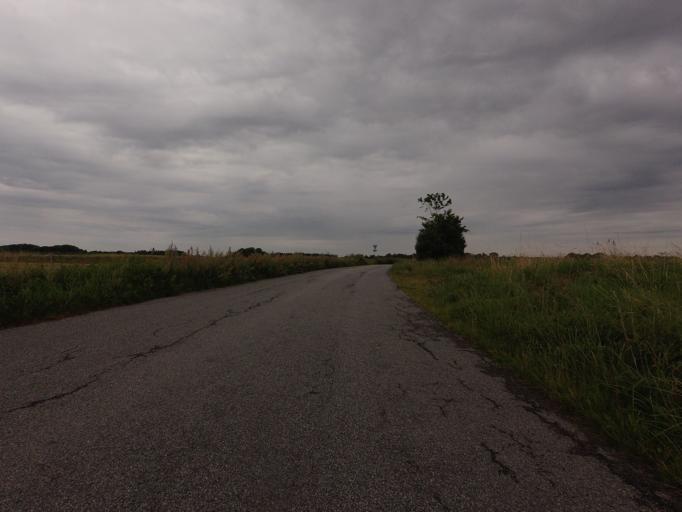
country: DK
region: North Denmark
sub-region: Alborg Kommune
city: Vadum
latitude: 57.1082
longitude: 9.8775
